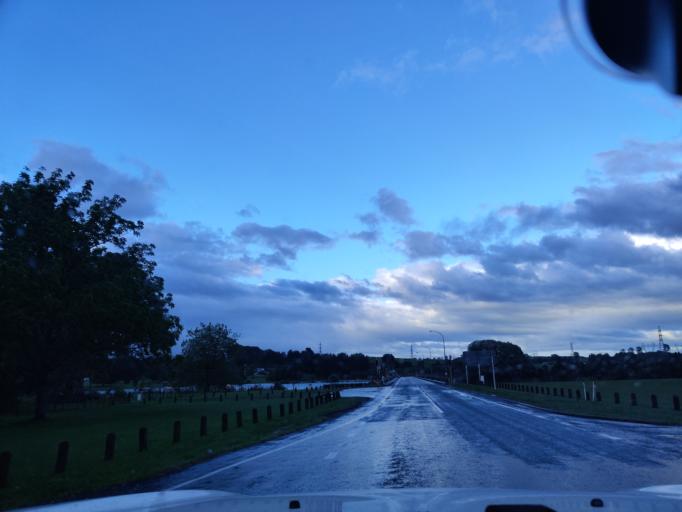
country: NZ
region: Waikato
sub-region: South Waikato District
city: Tokoroa
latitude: -38.4188
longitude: 175.8104
